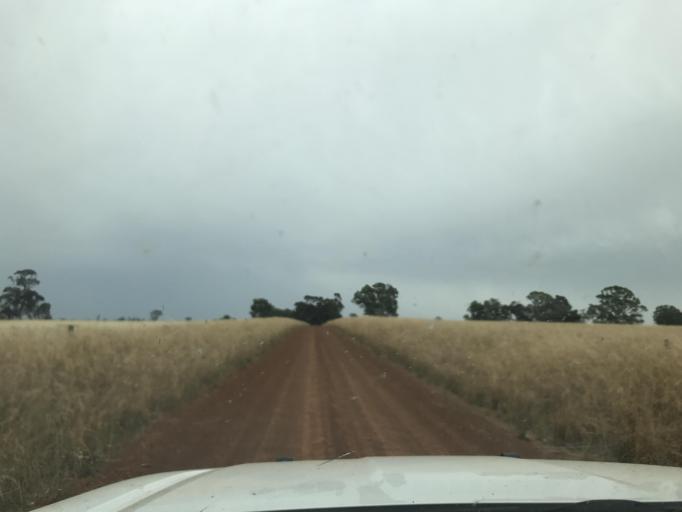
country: AU
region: Victoria
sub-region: Horsham
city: Horsham
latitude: -37.0663
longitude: 141.6689
